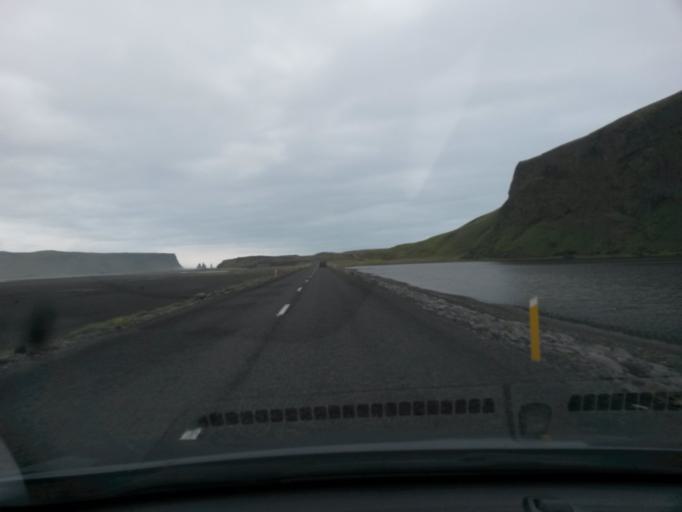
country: IS
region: South
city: Vestmannaeyjar
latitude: 63.4119
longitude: -19.1319
